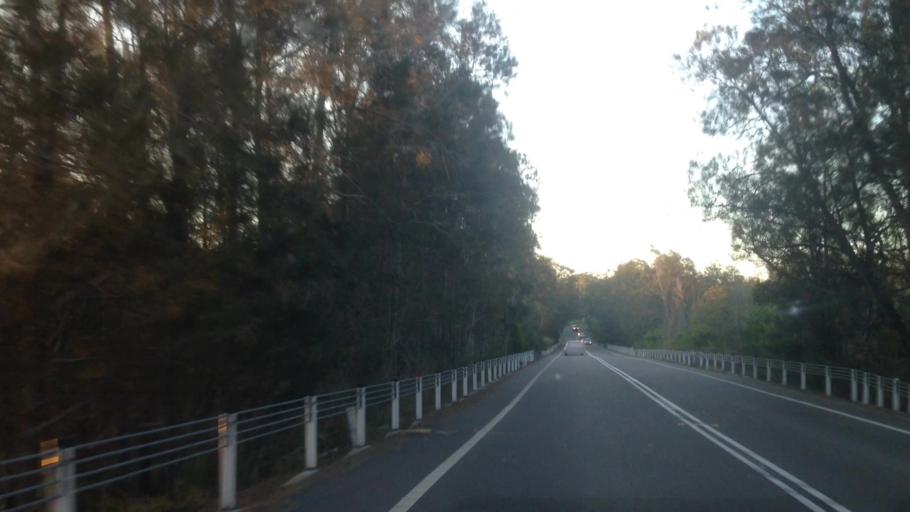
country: AU
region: New South Wales
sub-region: Wyong Shire
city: Kingfisher Shores
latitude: -33.1561
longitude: 151.5263
